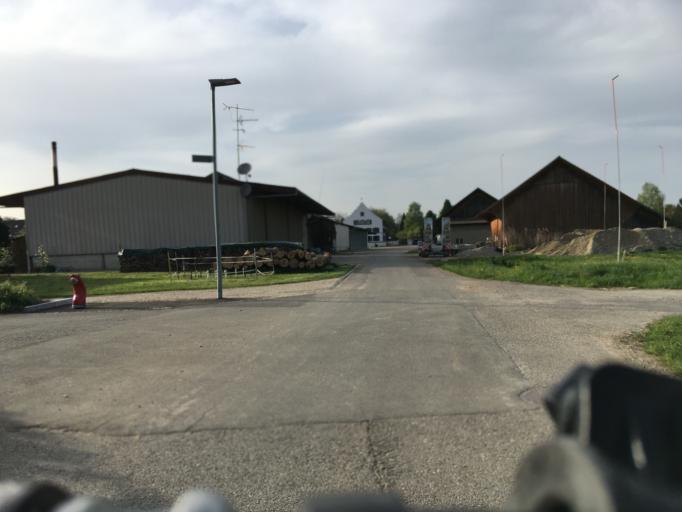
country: CH
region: Schaffhausen
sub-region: Bezirk Stein
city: Ramsen
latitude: 47.7055
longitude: 8.8080
